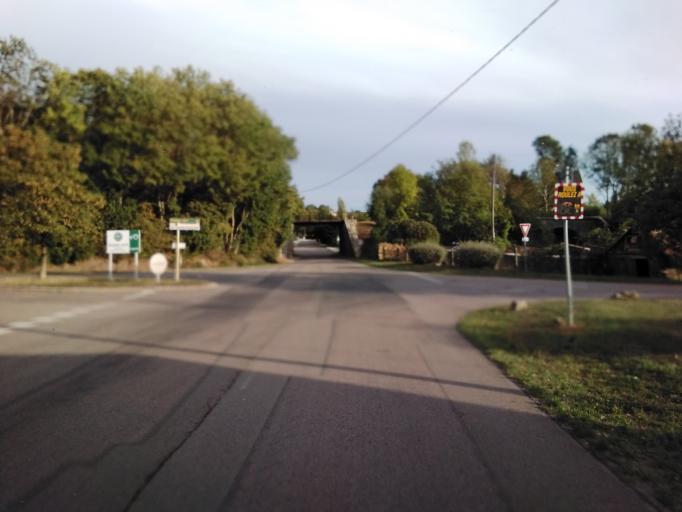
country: FR
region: Champagne-Ardenne
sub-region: Departement de l'Aube
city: Les Riceys
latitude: 47.8493
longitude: 4.3619
